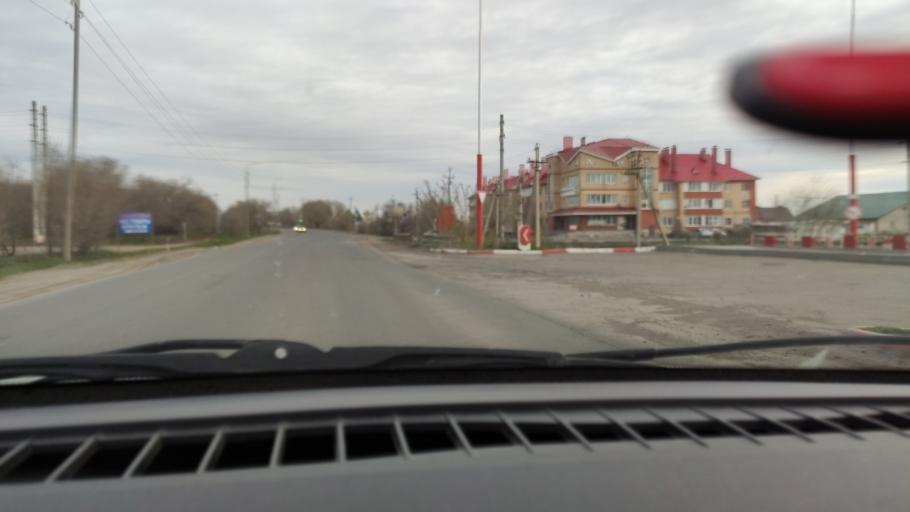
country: RU
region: Orenburg
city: Tatarskaya Kargala
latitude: 51.8789
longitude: 55.1490
